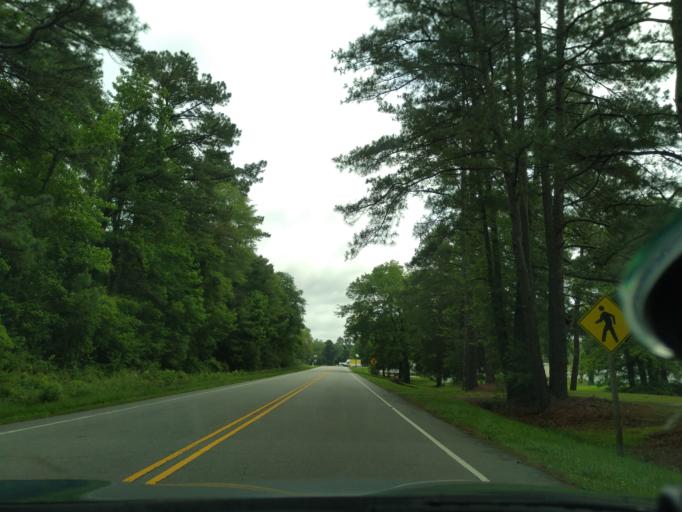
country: US
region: North Carolina
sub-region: Washington County
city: Plymouth
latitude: 35.8772
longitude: -76.6179
